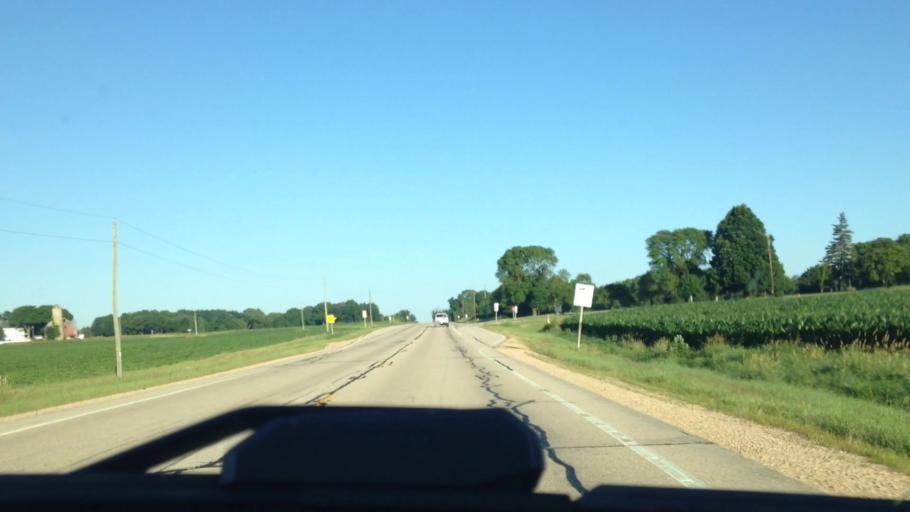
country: US
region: Wisconsin
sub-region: Columbia County
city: Rio
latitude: 43.3404
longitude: -89.1706
